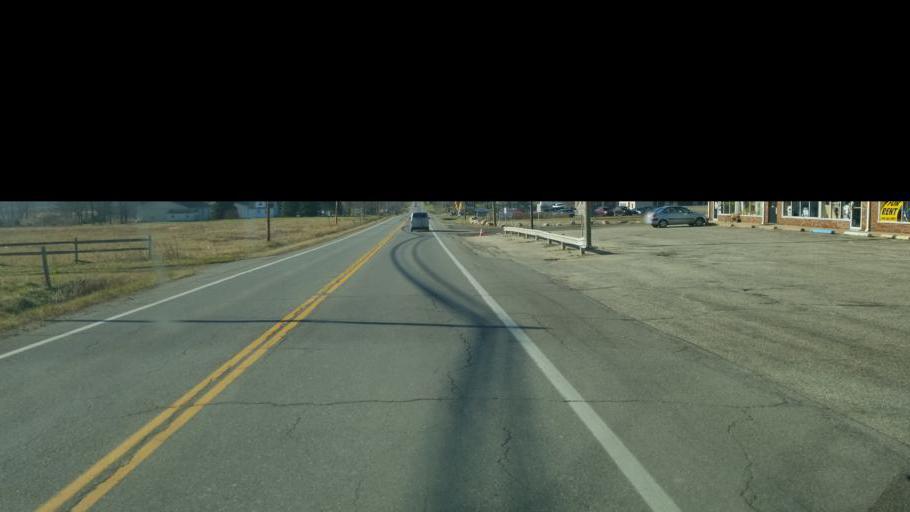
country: US
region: Ohio
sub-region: Geauga County
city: Burton
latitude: 41.4634
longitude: -81.2313
